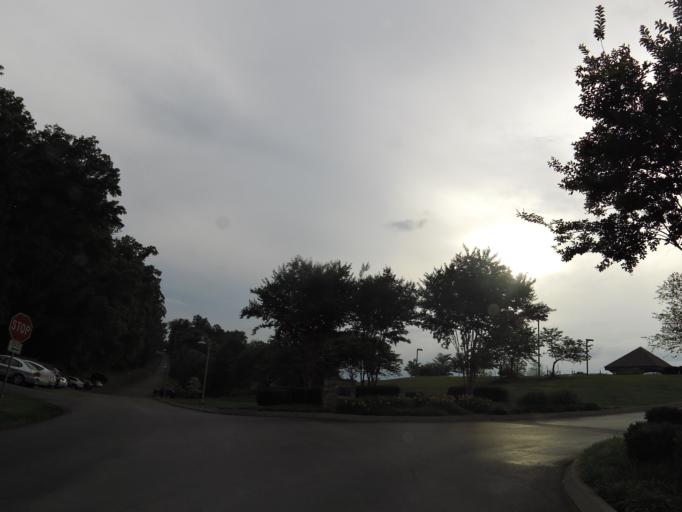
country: US
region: Tennessee
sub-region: Knox County
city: Farragut
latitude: 35.8648
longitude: -84.1286
